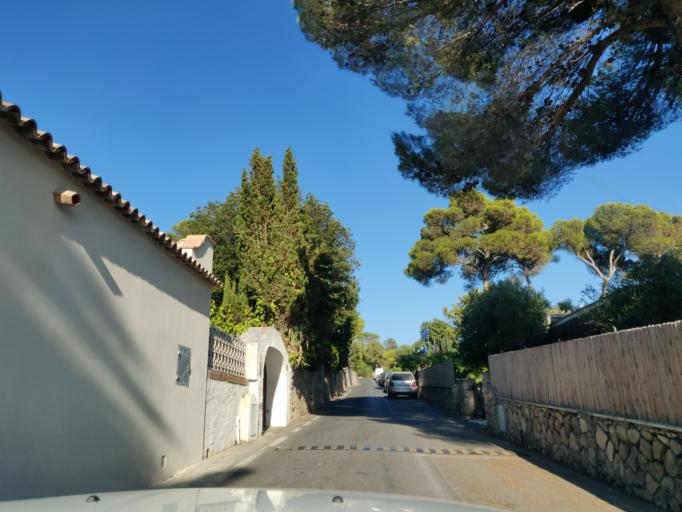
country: IT
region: Tuscany
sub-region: Provincia di Grosseto
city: Orbetello Scalo
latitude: 42.4073
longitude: 11.2870
